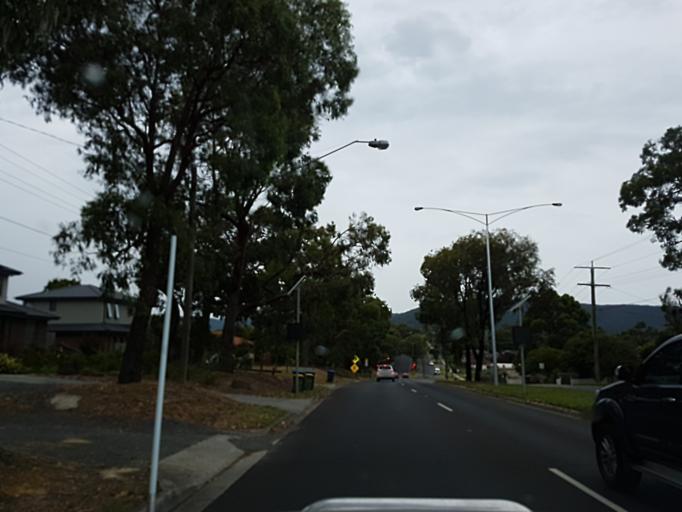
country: AU
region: Victoria
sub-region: Knox
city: Bayswater
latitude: -37.8610
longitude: 145.2717
